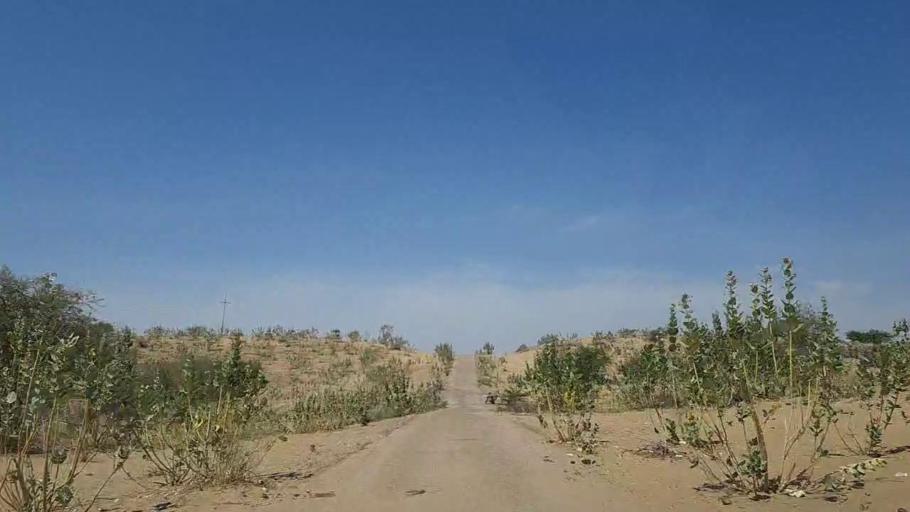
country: PK
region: Sindh
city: Mithi
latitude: 24.8579
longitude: 69.6696
